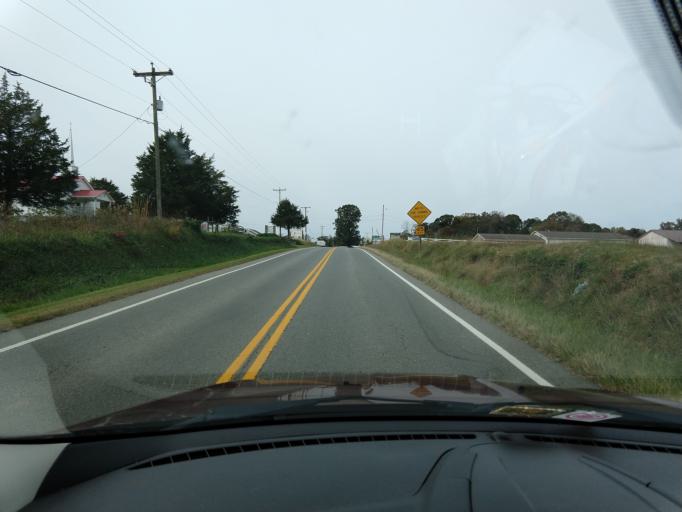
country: US
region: Virginia
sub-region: Franklin County
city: Union Hall
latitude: 36.9932
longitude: -79.6826
